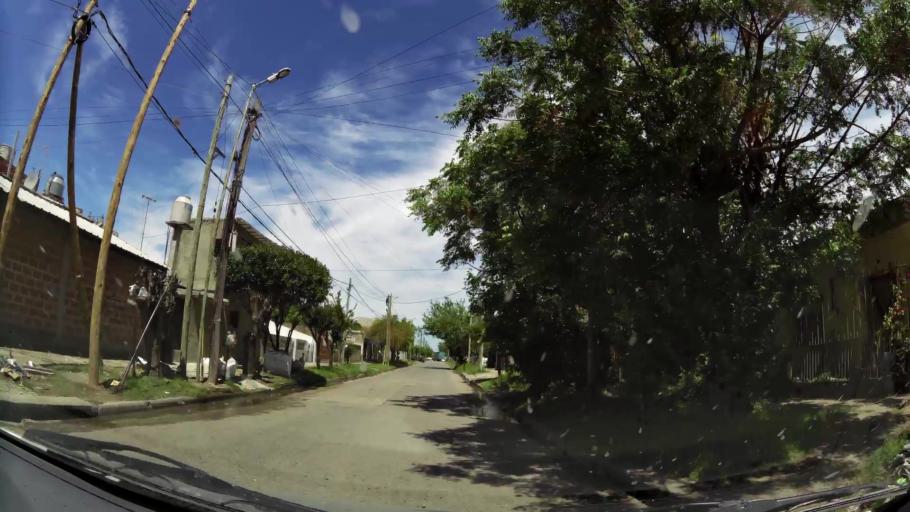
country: AR
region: Buenos Aires
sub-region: Partido de Quilmes
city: Quilmes
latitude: -34.7401
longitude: -58.3035
